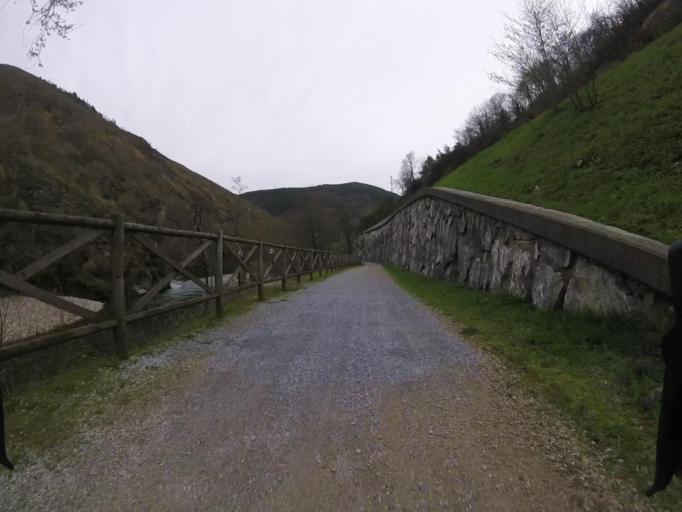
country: ES
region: Navarre
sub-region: Provincia de Navarra
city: Bera
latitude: 43.2962
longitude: -1.7308
